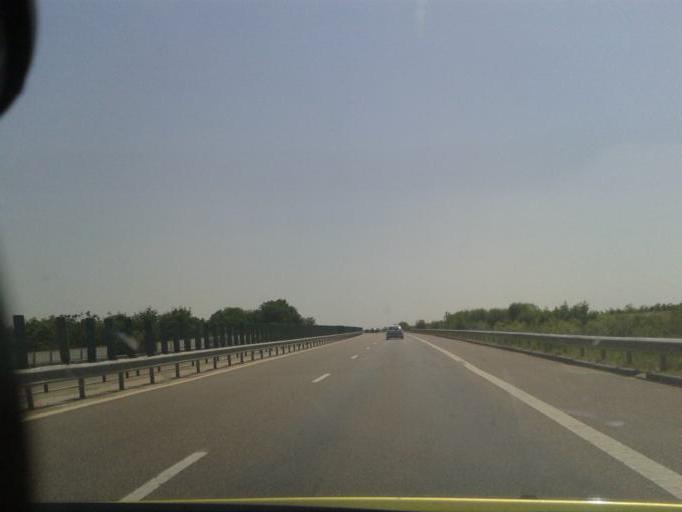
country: RO
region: Calarasi
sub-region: Comuna Sarulesti
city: Sarulesti-Gara
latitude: 44.4399
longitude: 26.6502
